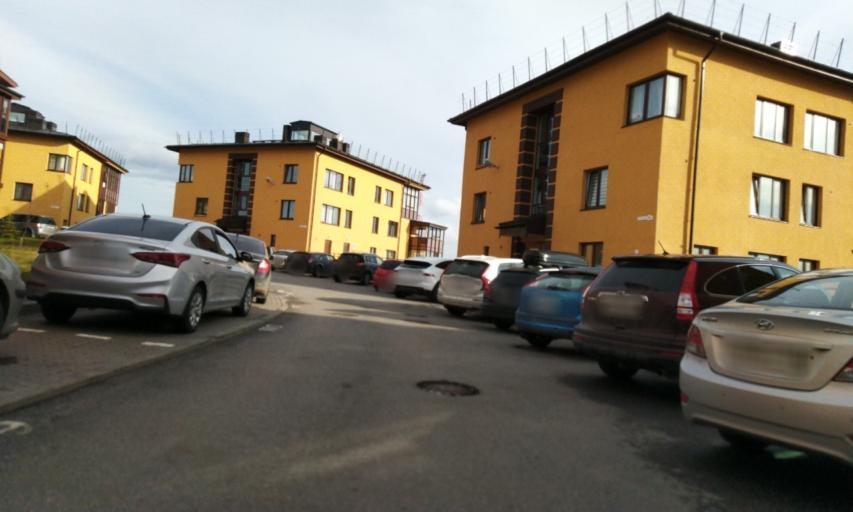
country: RU
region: Leningrad
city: Bugry
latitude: 60.1198
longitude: 30.4184
